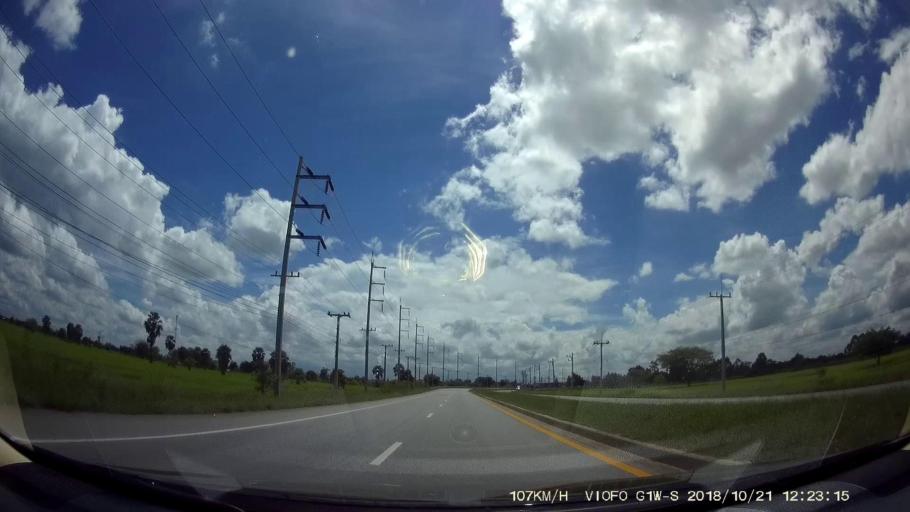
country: TH
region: Nakhon Ratchasima
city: Dan Khun Thot
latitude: 15.2483
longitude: 101.7887
